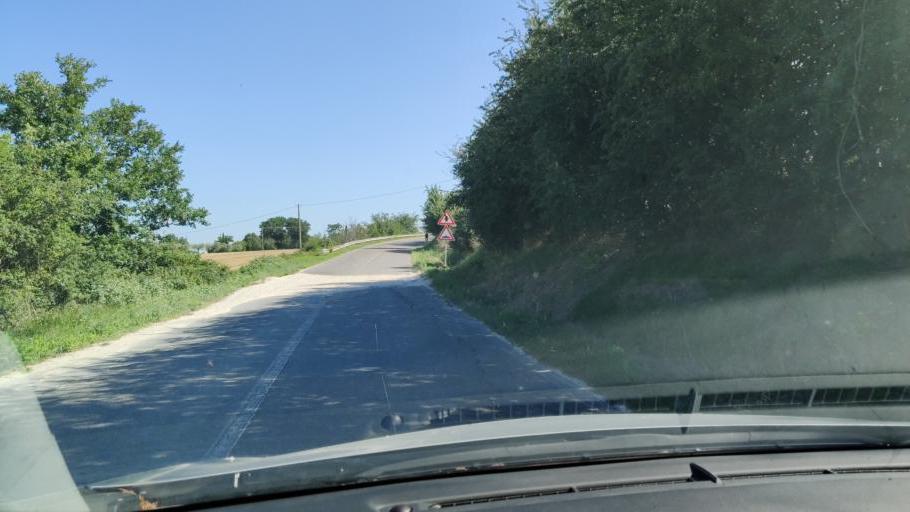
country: IT
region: Umbria
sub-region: Provincia di Terni
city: Avigliano Umbro
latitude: 42.6976
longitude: 12.4524
